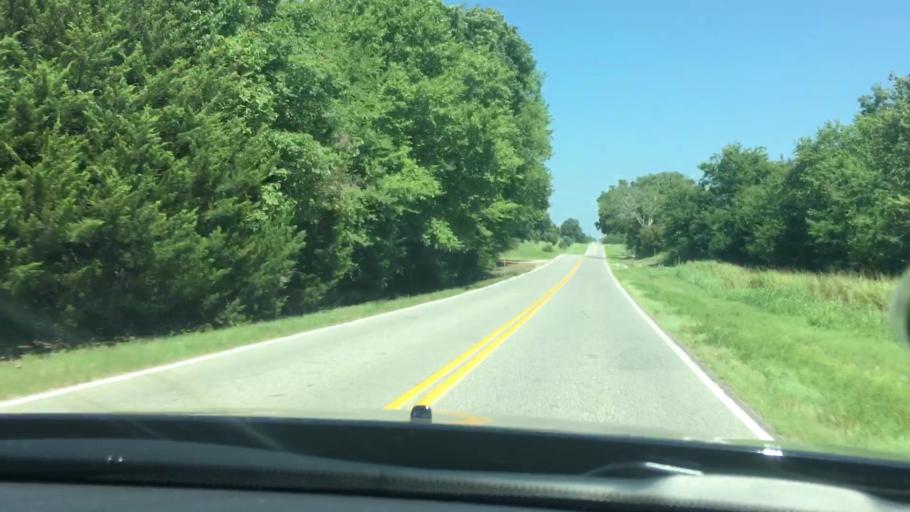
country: US
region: Oklahoma
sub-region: Johnston County
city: Tishomingo
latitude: 34.2658
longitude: -96.5487
